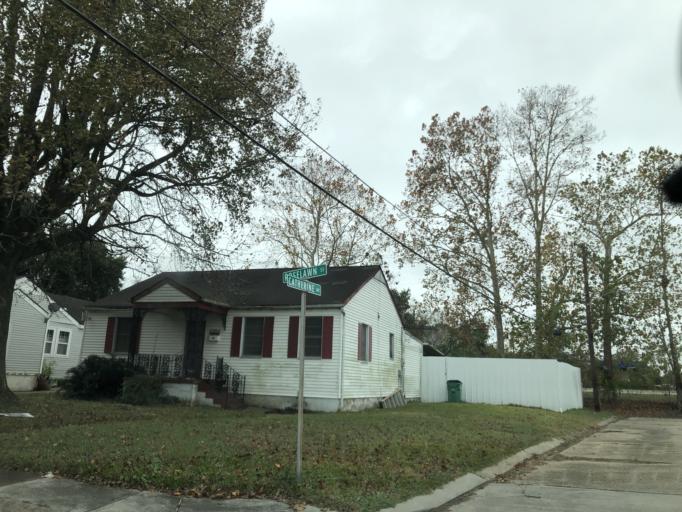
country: US
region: Louisiana
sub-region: Jefferson Parish
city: Metairie Terrace
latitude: 29.9741
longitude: -90.1689
